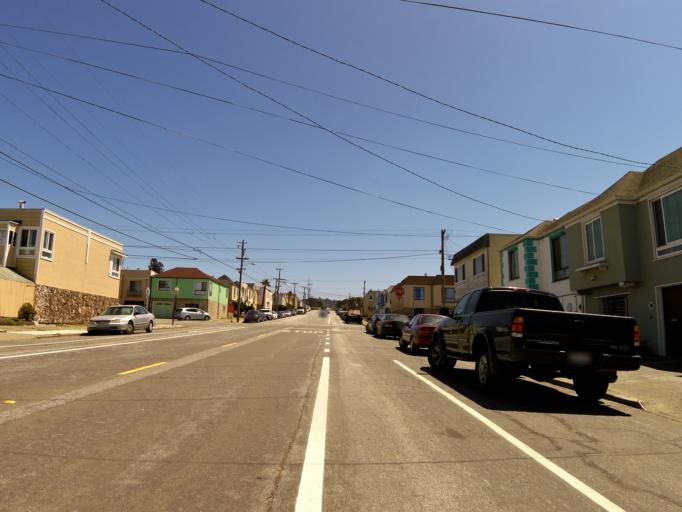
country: US
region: California
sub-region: San Mateo County
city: Daly City
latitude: 37.7511
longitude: -122.5048
